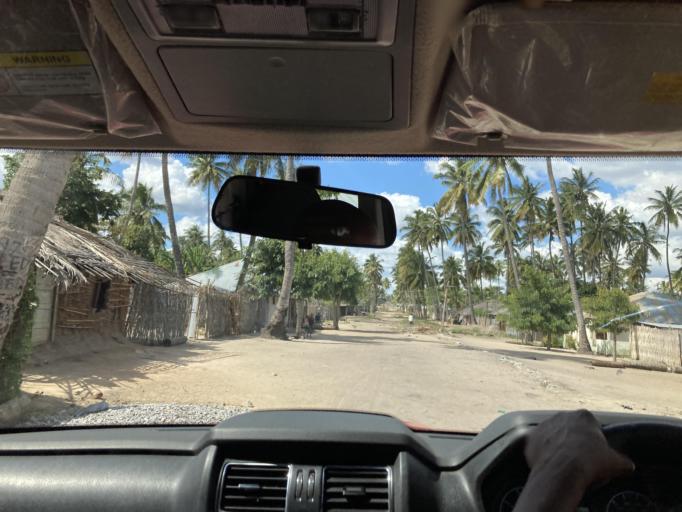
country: MZ
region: Cabo Delgado
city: Montepuez
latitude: -13.1303
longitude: 39.0088
